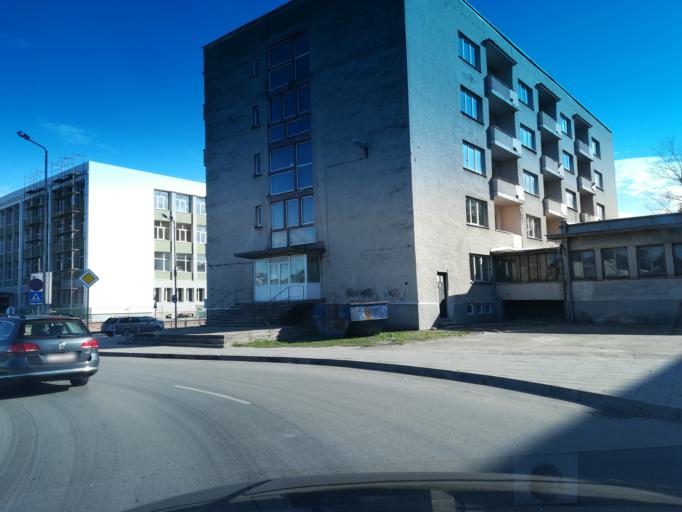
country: BG
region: Stara Zagora
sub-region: Obshtina Stara Zagora
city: Stara Zagora
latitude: 42.4314
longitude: 25.6390
